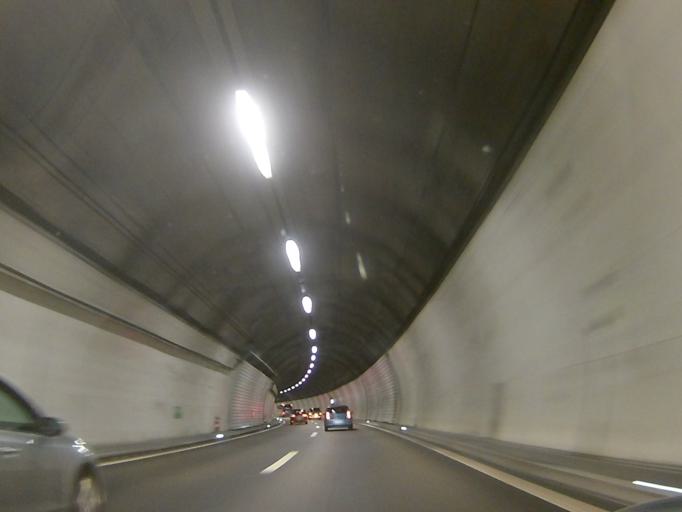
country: CH
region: Ticino
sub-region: Lugano District
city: Melide
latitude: 45.9603
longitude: 8.9428
